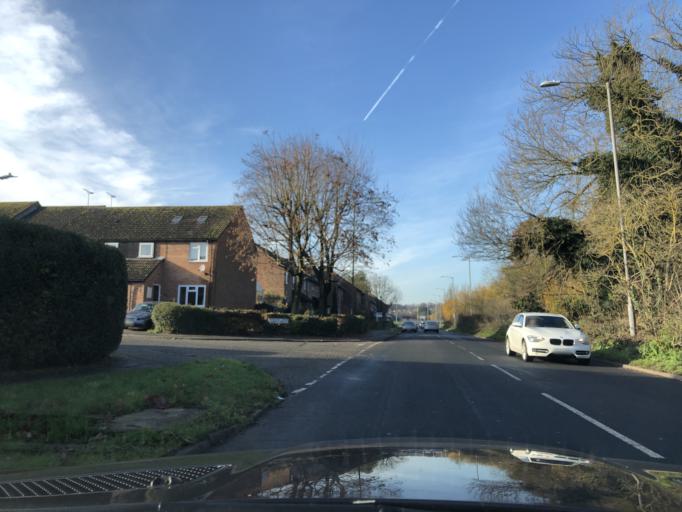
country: GB
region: England
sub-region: Buckinghamshire
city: Marlow
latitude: 51.5838
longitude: -0.7621
